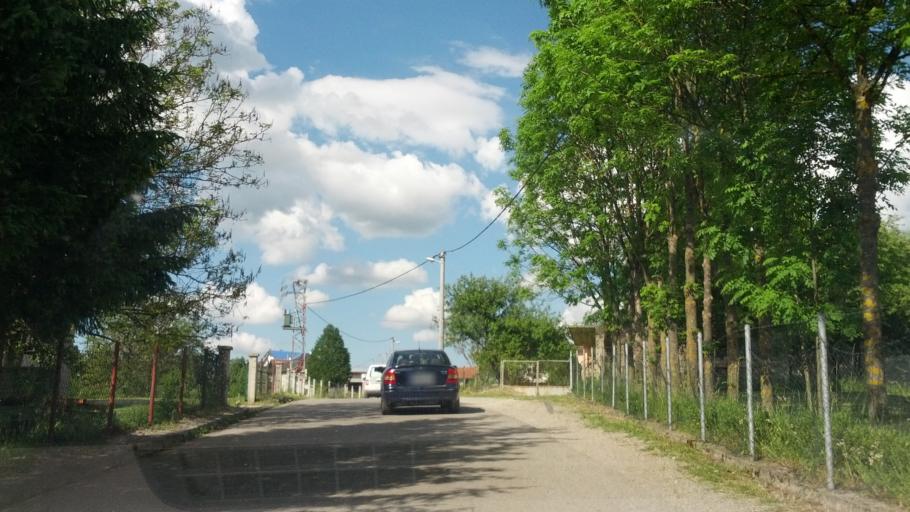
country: BA
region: Federation of Bosnia and Herzegovina
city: Ostrozac
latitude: 44.9213
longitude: 15.9546
